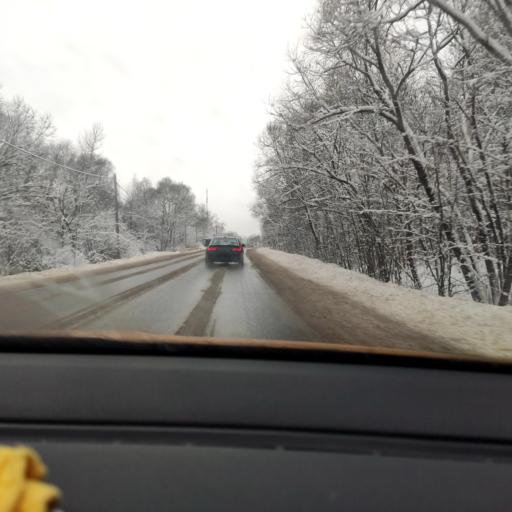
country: RU
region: Moskovskaya
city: Yershovo
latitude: 55.7626
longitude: 36.8630
